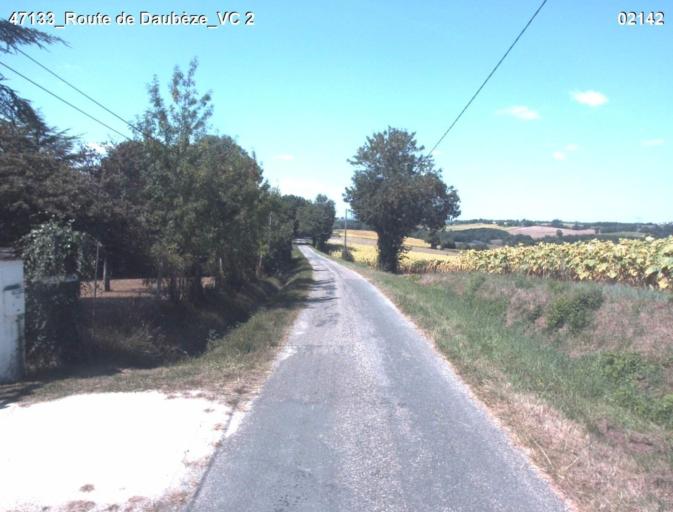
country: FR
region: Aquitaine
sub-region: Departement du Lot-et-Garonne
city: Laplume
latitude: 44.0787
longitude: 0.5580
